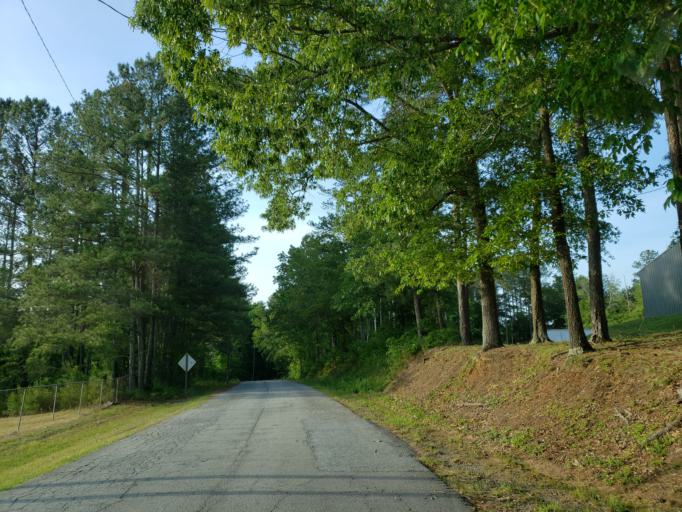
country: US
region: Georgia
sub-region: Carroll County
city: Mount Zion
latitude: 33.6352
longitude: -85.1856
